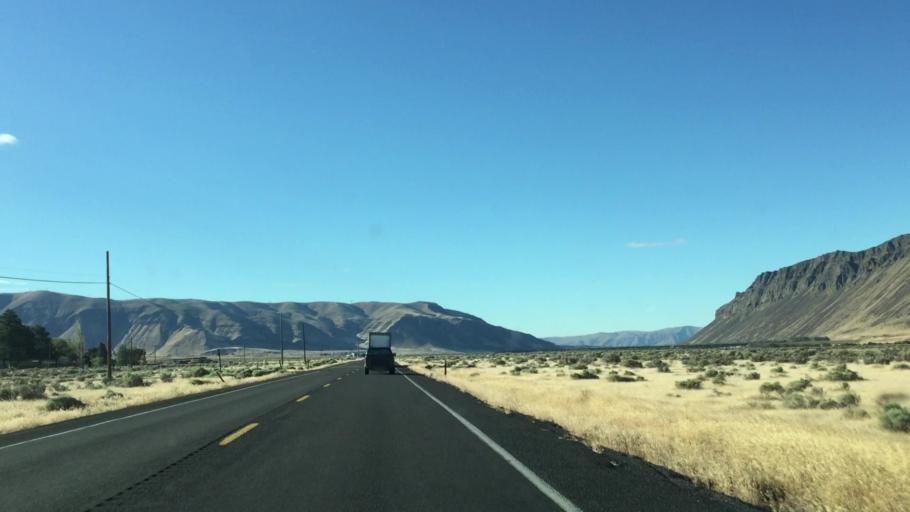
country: US
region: Washington
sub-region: Grant County
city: Mattawa
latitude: 46.8635
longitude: -119.9518
